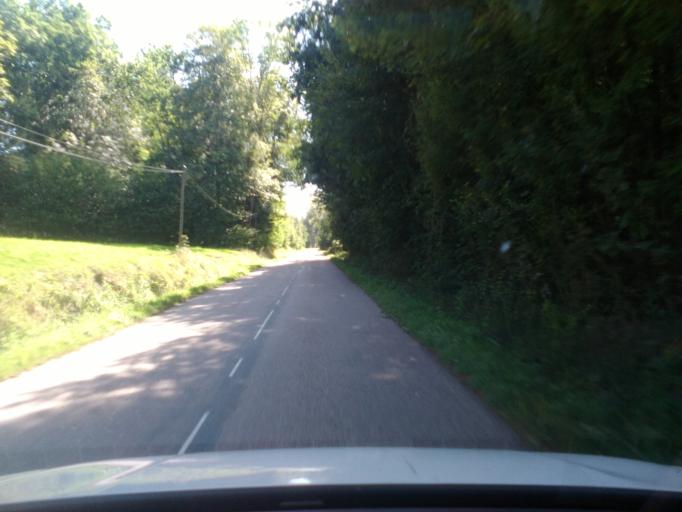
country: FR
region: Lorraine
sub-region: Departement des Vosges
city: Senones
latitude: 48.3844
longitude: 6.9621
